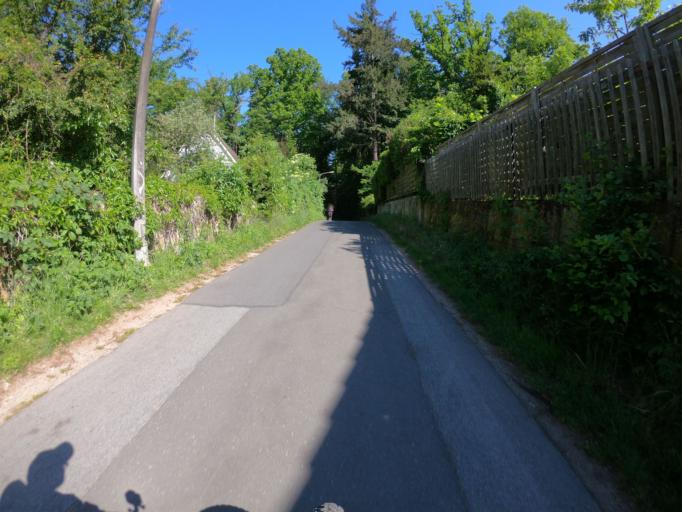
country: DE
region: Bavaria
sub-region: Regierungsbezirk Mittelfranken
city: Stein
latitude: 49.4120
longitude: 11.0217
